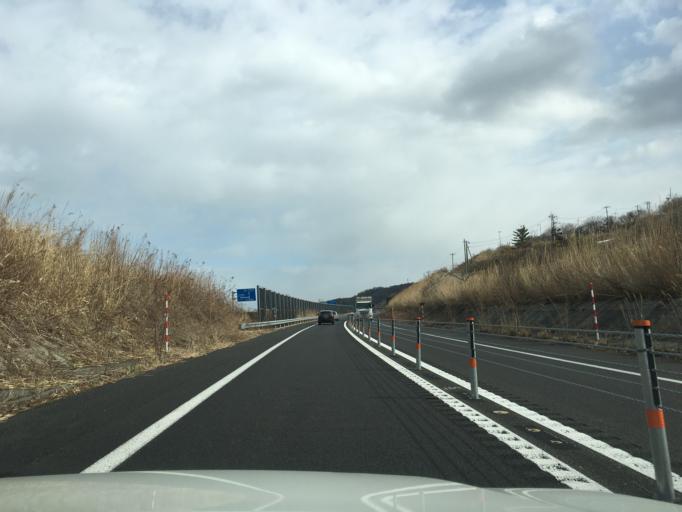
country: JP
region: Yamagata
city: Yuza
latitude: 39.3039
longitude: 139.9783
